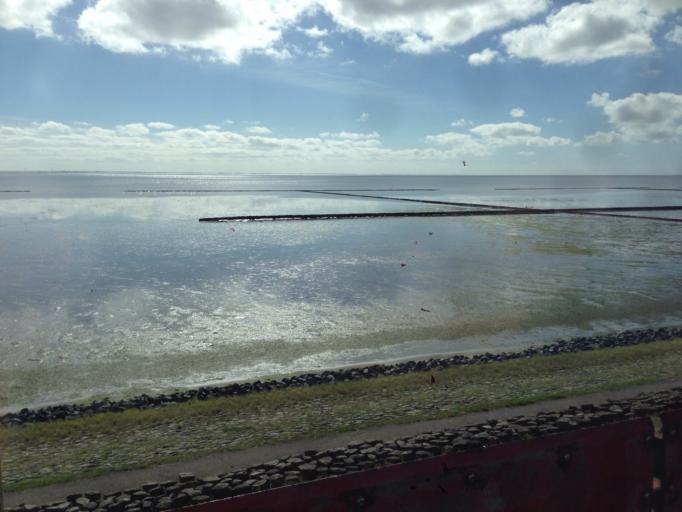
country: DE
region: Schleswig-Holstein
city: Friedrich-Wilhelm-Lubke-Koog
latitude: 54.8841
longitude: 8.5412
